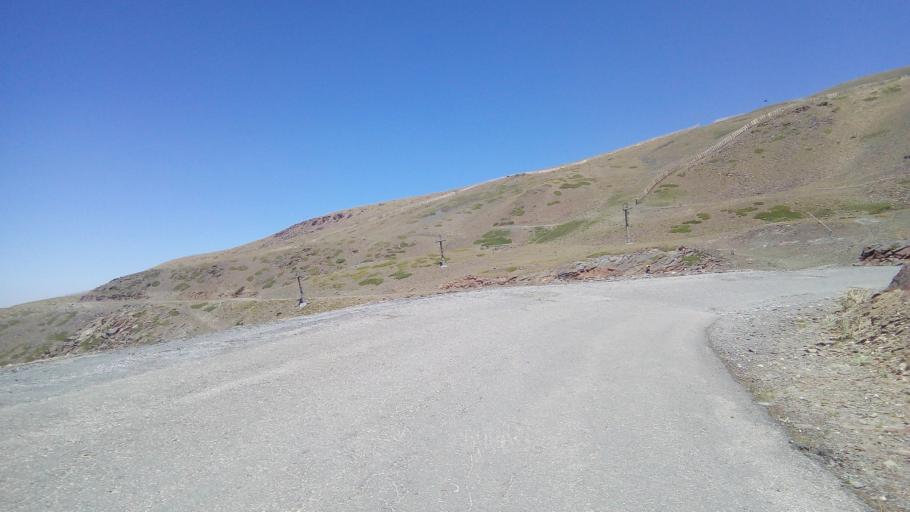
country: ES
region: Andalusia
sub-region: Provincia de Granada
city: Guejar-Sierra
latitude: 37.0719
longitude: -3.3871
